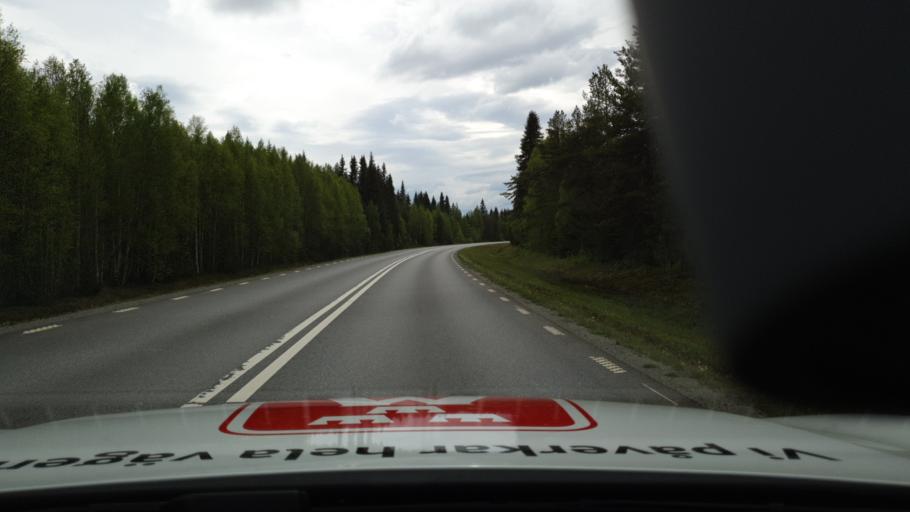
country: SE
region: Vaesterbotten
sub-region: Vilhelmina Kommun
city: Vilhelmina
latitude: 64.3608
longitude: 16.7063
